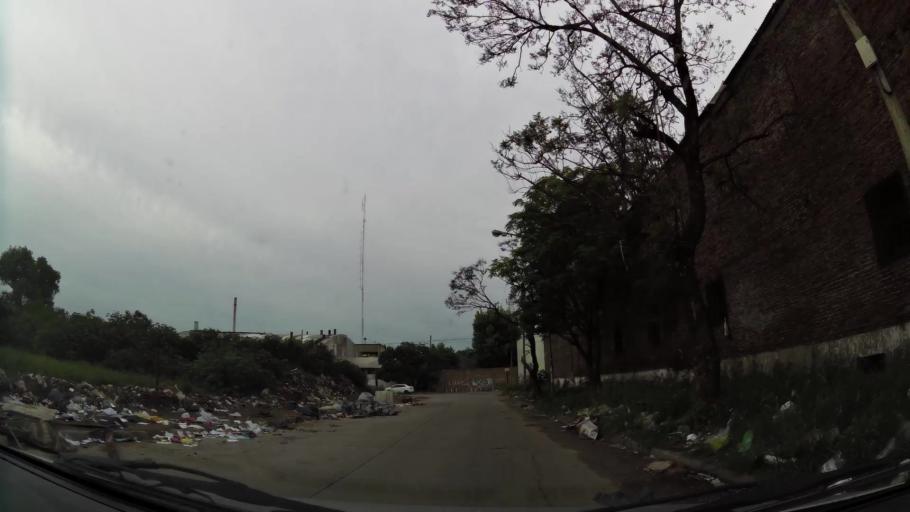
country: AR
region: Buenos Aires
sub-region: Partido de Lanus
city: Lanus
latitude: -34.7122
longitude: -58.3647
